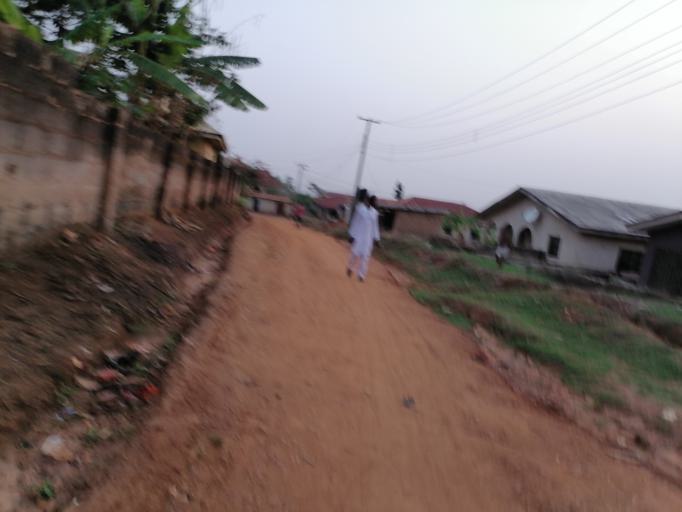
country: NG
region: Ondo
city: Akure
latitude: 7.2866
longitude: 5.1483
